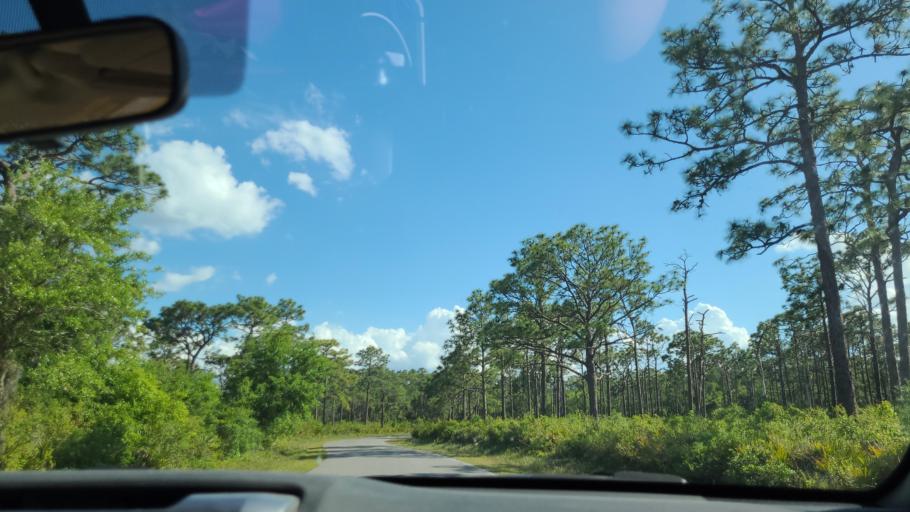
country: US
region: Florida
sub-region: Polk County
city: Babson Park
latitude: 27.9571
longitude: -81.3757
